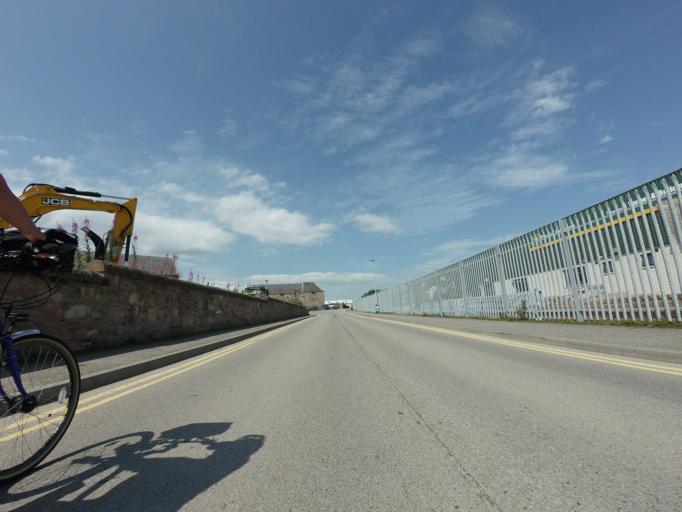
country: GB
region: Scotland
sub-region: Highland
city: Tain
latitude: 57.8151
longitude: -4.0556
